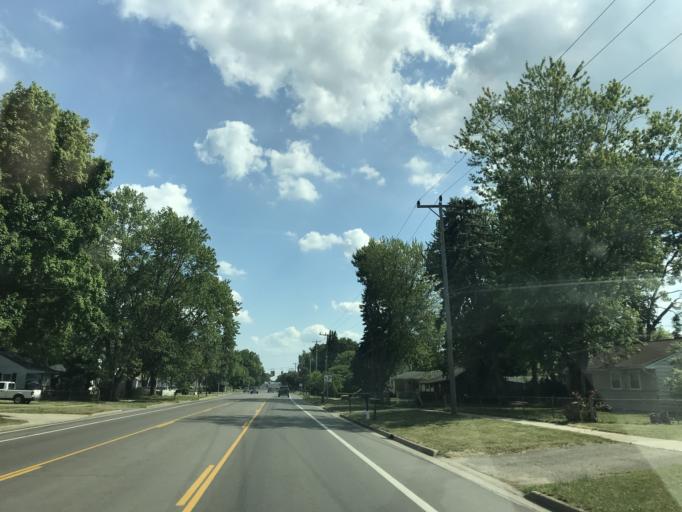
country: US
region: Michigan
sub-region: Washtenaw County
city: Ypsilanti
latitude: 42.2518
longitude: -83.5806
